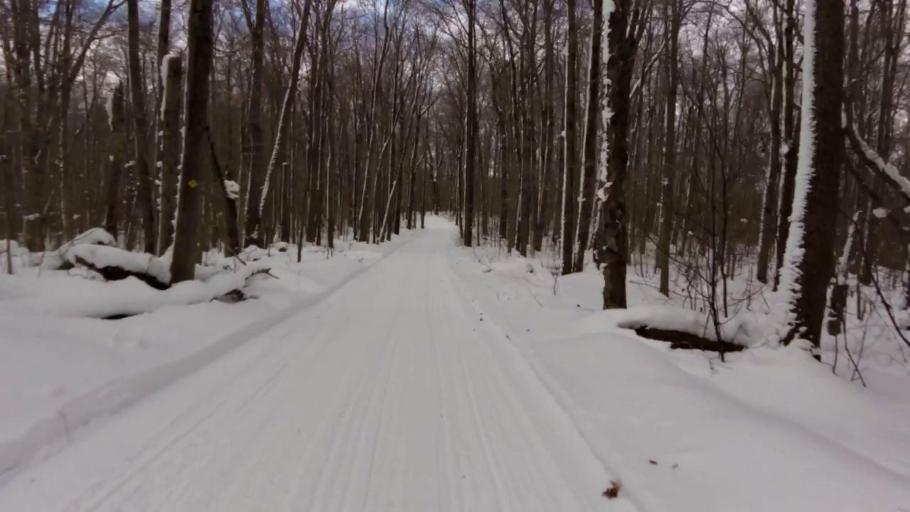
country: US
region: New York
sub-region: Cattaraugus County
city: Salamanca
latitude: 42.0488
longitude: -78.7600
